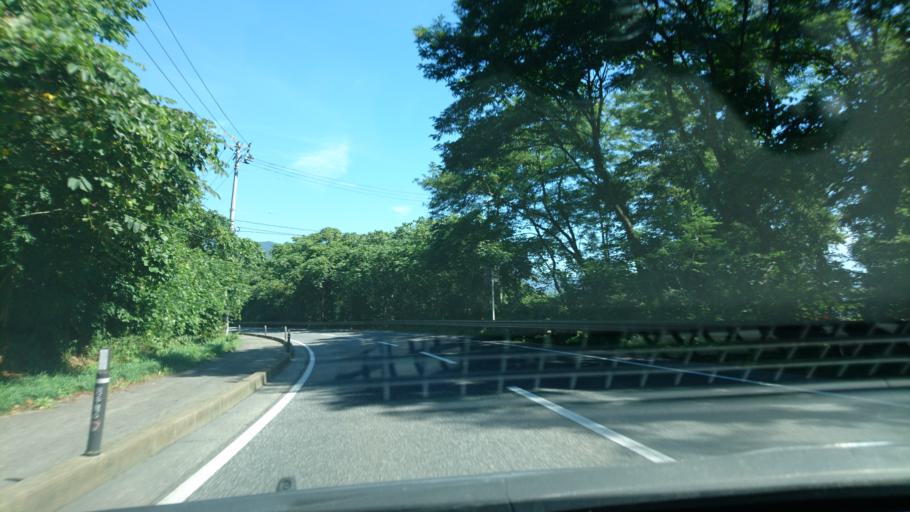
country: JP
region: Iwate
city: Tono
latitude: 39.3346
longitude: 141.5192
